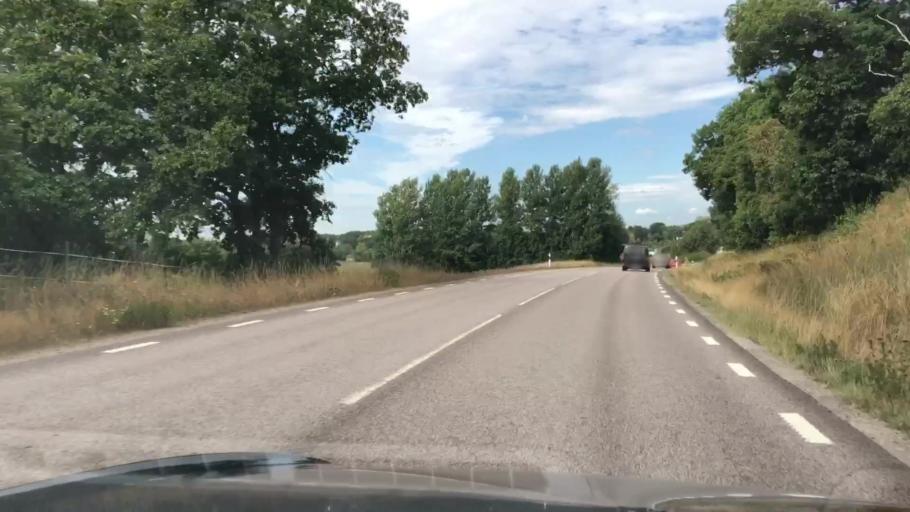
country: SE
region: Blekinge
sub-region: Karlskrona Kommun
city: Sturko
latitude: 56.1913
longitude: 15.7033
